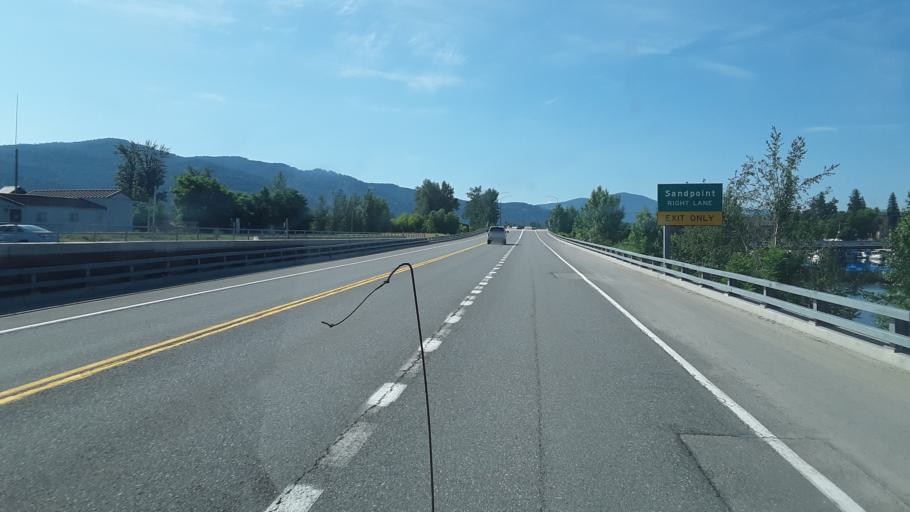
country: US
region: Idaho
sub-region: Bonner County
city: Sandpoint
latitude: 48.2762
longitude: -116.5459
